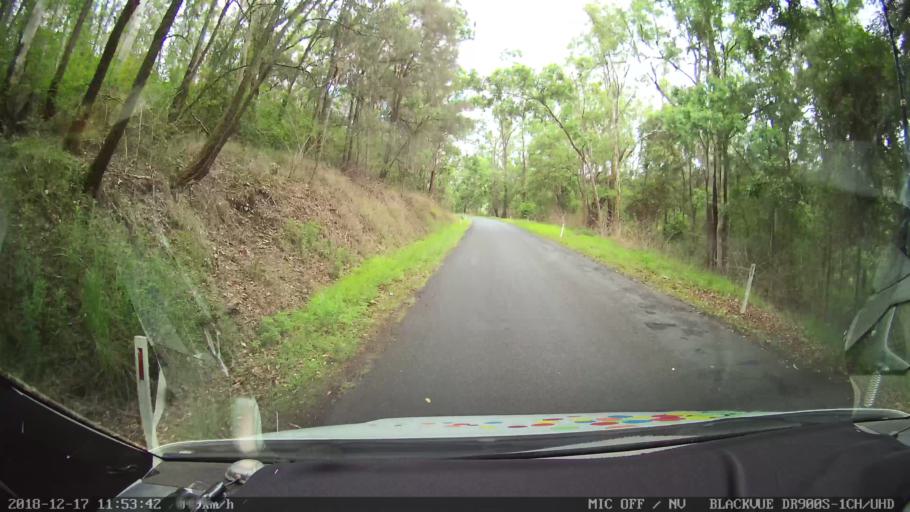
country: AU
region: New South Wales
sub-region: Kyogle
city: Kyogle
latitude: -28.5725
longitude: 152.5857
